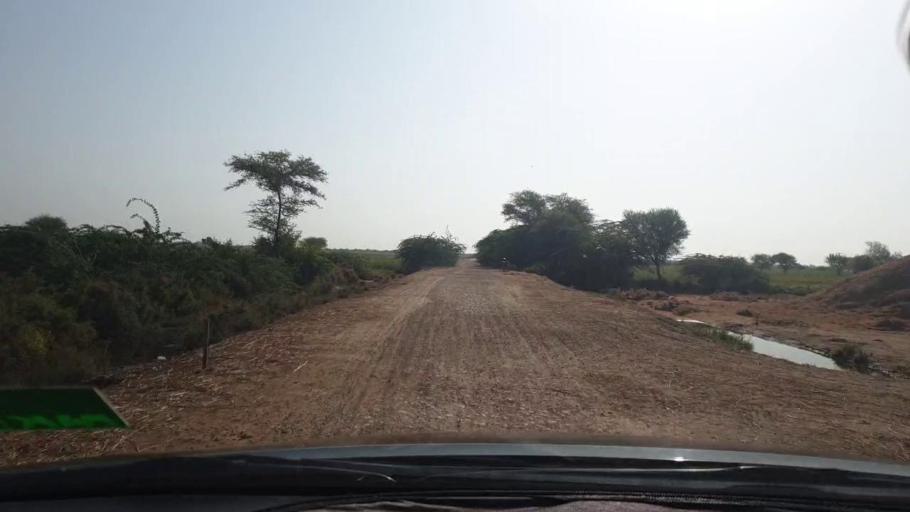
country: PK
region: Sindh
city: Tando Bago
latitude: 24.7190
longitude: 68.9623
